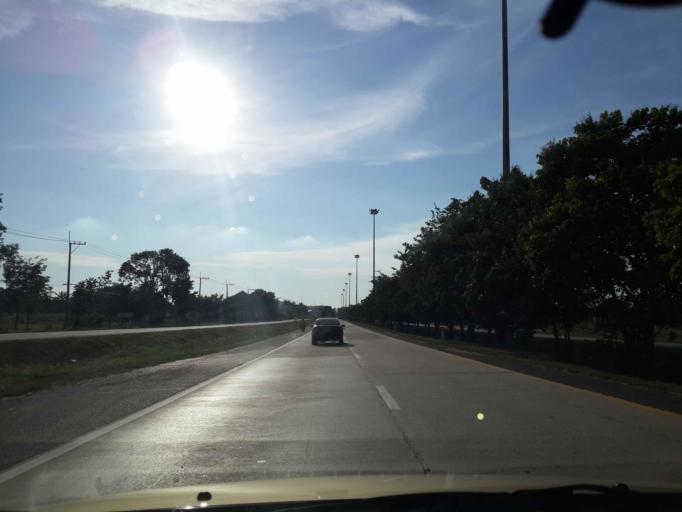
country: TH
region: Chon Buri
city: Bang Lamung
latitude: 12.9670
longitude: 100.9780
